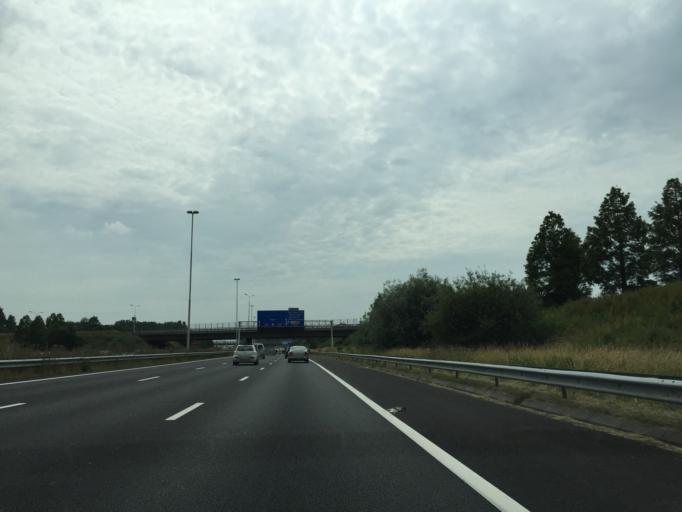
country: NL
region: South Holland
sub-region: Gemeente Rijswijk
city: Rijswijk
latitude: 52.0283
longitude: 4.3249
